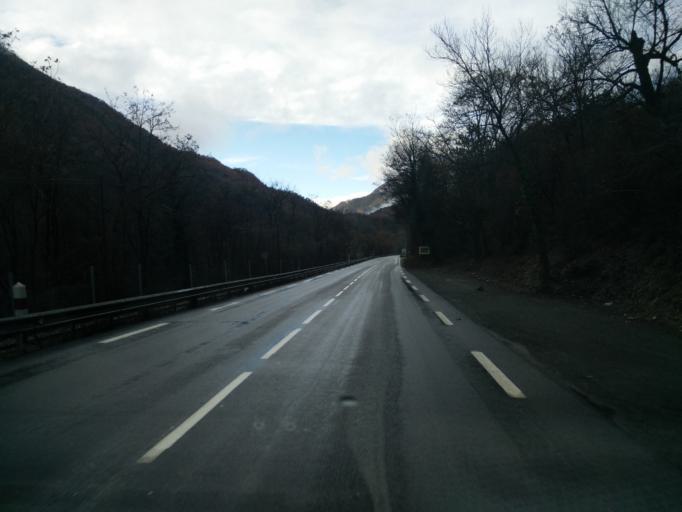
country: FR
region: Provence-Alpes-Cote d'Azur
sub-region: Departement des Alpes-Maritimes
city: Gilette
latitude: 43.9290
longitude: 7.0942
